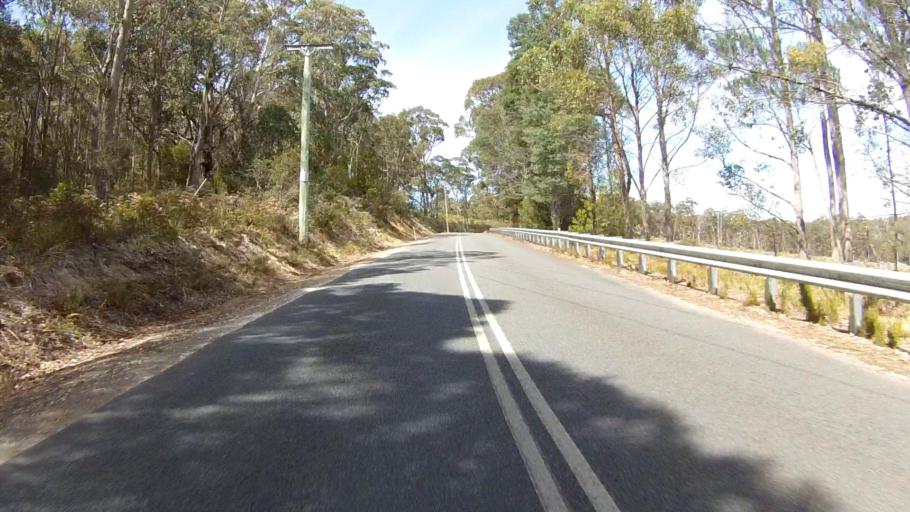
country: AU
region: Tasmania
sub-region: Huon Valley
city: Cygnet
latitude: -43.2229
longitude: 147.1283
